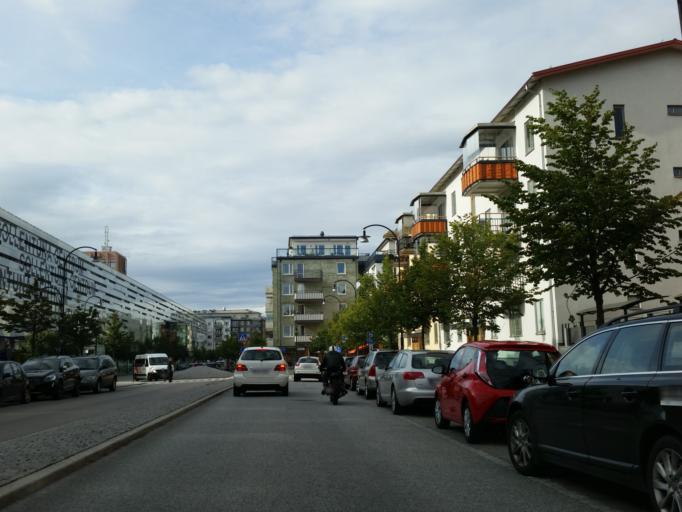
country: SE
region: Stockholm
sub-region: Sollentuna Kommun
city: Sollentuna
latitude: 59.4272
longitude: 17.9541
